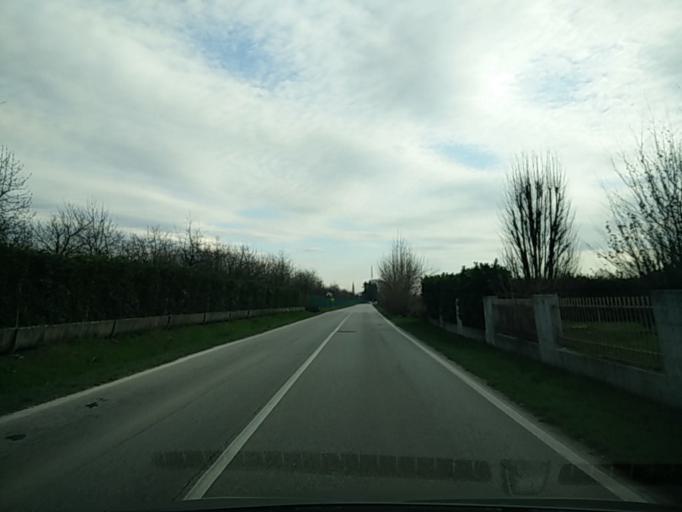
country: IT
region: Veneto
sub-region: Provincia di Treviso
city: Paese
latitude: 45.6809
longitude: 12.1735
